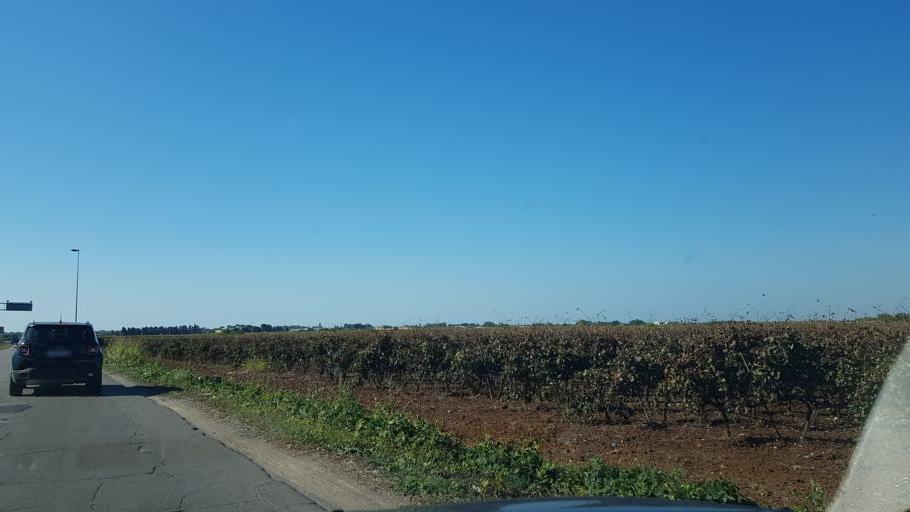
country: IT
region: Apulia
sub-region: Provincia di Lecce
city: Leverano
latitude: 40.2937
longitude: 17.9871
